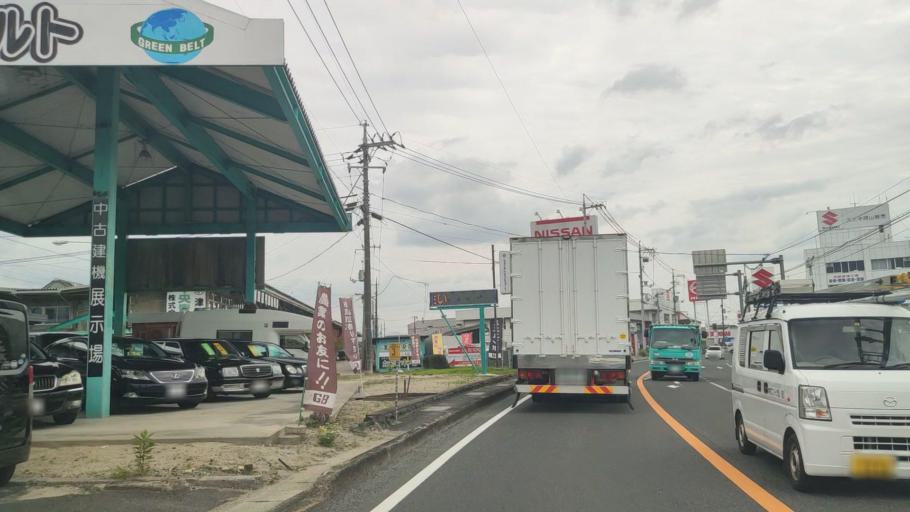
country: JP
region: Okayama
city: Tsuyama
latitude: 35.0577
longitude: 133.9817
